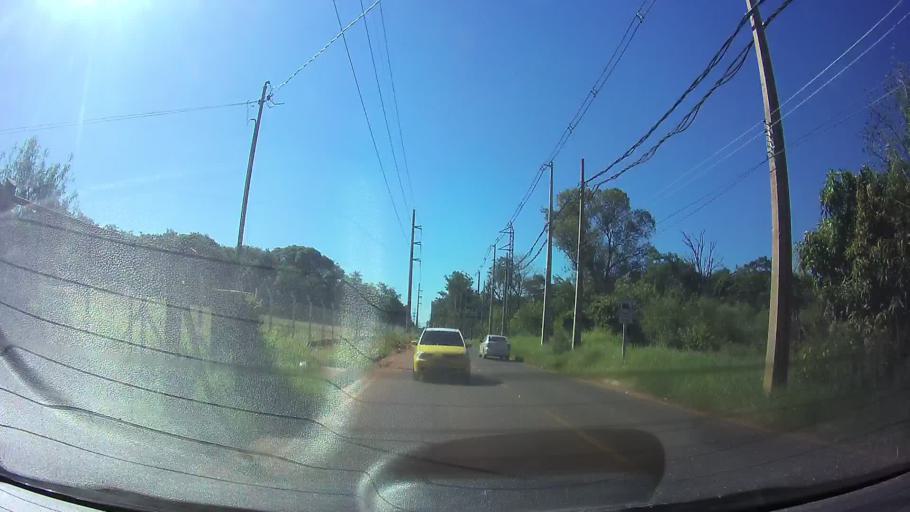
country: PY
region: Central
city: Fernando de la Mora
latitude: -25.3213
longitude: -57.5146
